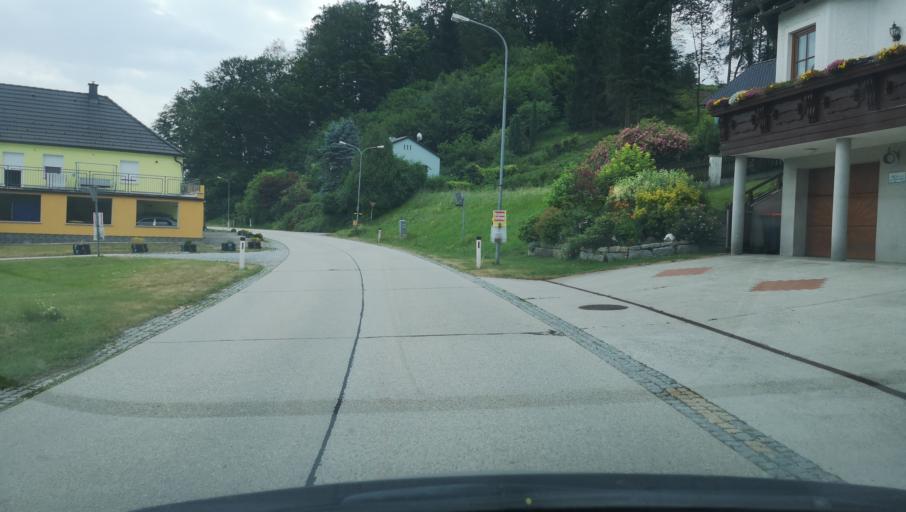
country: AT
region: Lower Austria
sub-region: Politischer Bezirk Melk
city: Ybbs an der Donau
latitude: 48.1902
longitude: 15.0612
